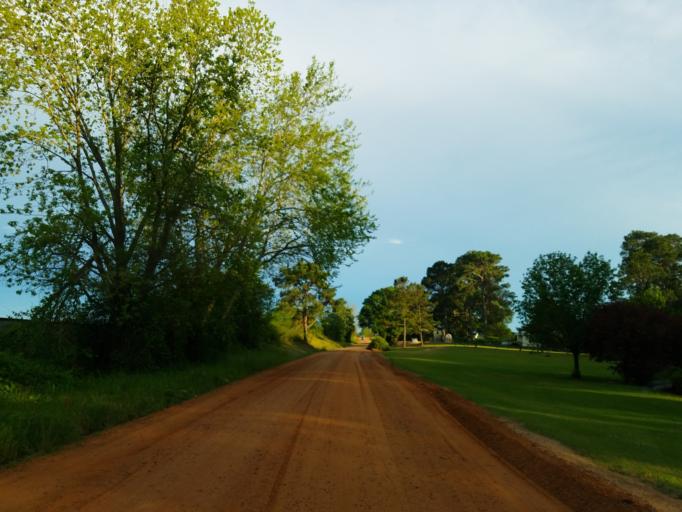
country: US
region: Georgia
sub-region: Turner County
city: Ashburn
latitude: 31.6464
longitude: -83.6213
